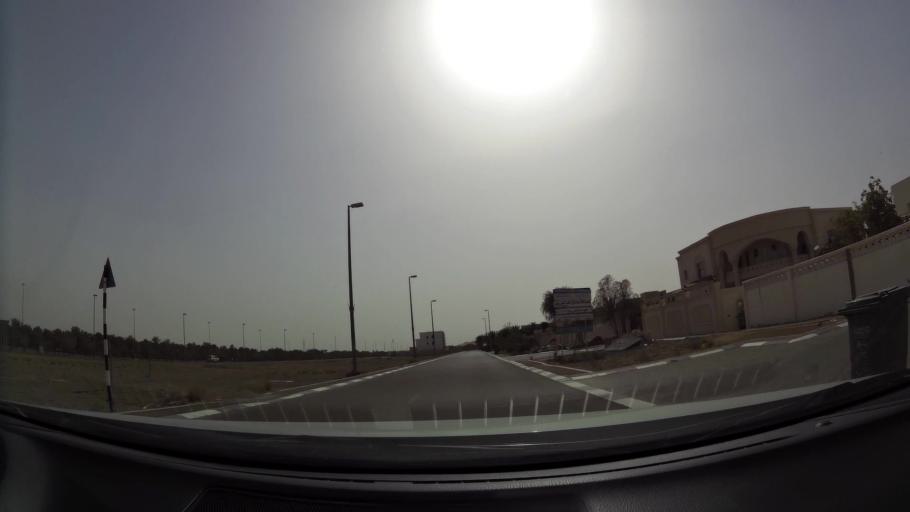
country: AE
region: Abu Dhabi
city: Al Ain
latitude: 24.2040
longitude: 55.5769
